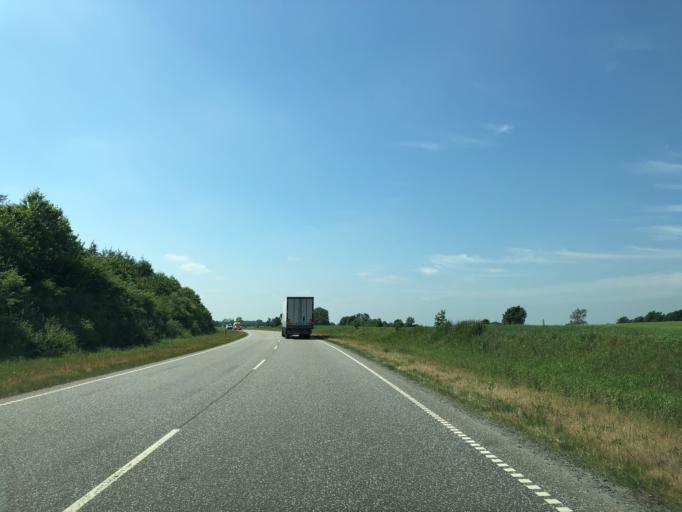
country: DK
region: South Denmark
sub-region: Kolding Kommune
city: Kolding
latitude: 55.5464
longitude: 9.4721
